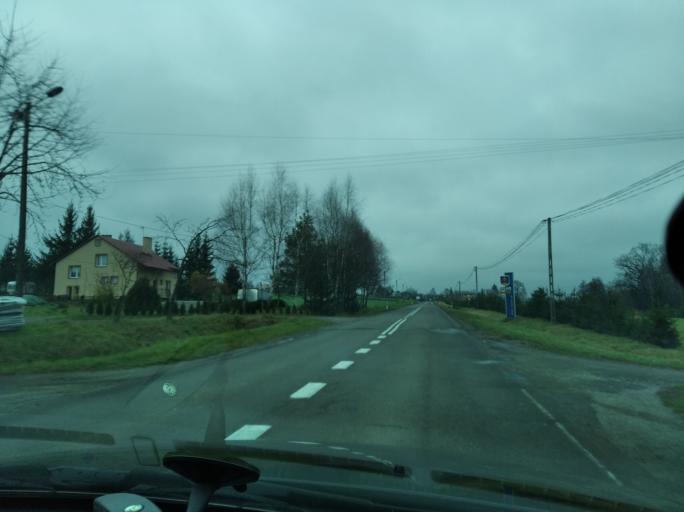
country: PL
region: Subcarpathian Voivodeship
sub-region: Powiat rzeszowski
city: Dynow
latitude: 49.8593
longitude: 22.2489
